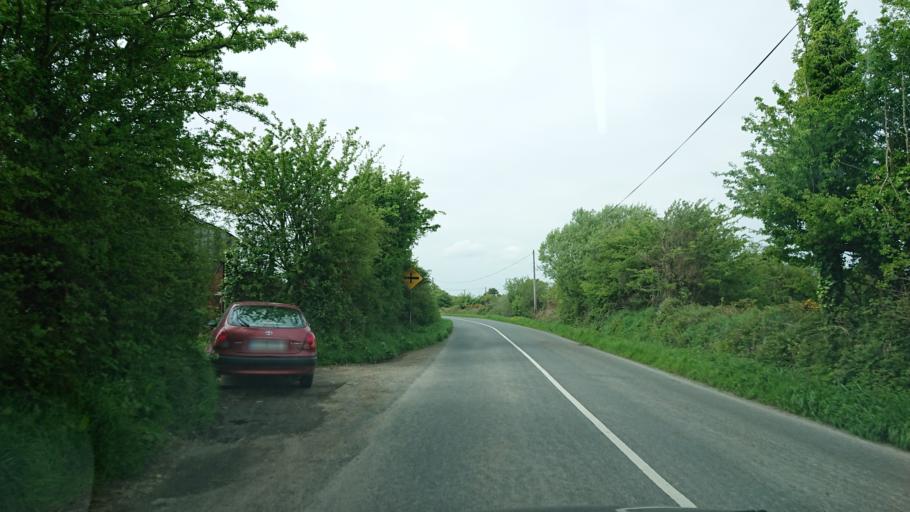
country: IE
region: Munster
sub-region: Waterford
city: Waterford
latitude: 52.2205
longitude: -7.0698
